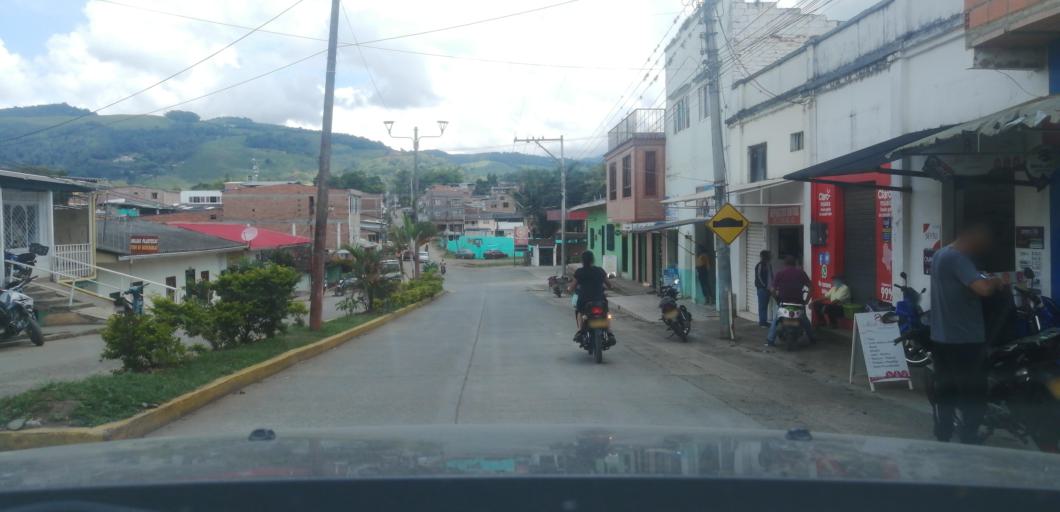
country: CO
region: Valle del Cauca
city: Restrepo
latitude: 3.8214
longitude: -76.5239
